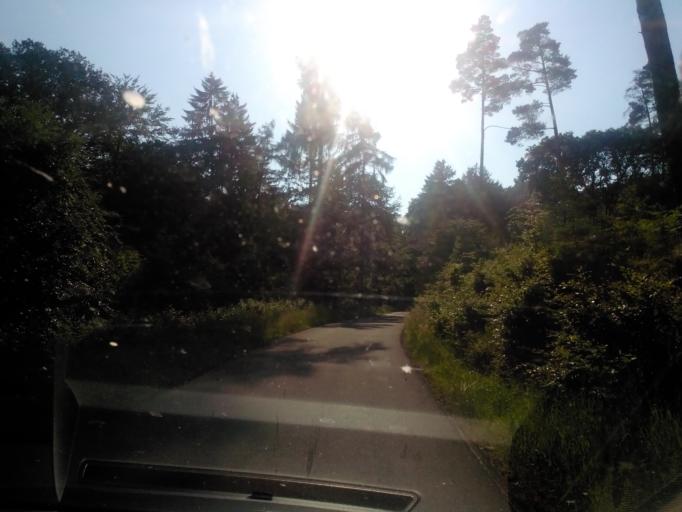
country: DE
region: Saarland
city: Nalbach
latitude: 49.4183
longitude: 6.8075
